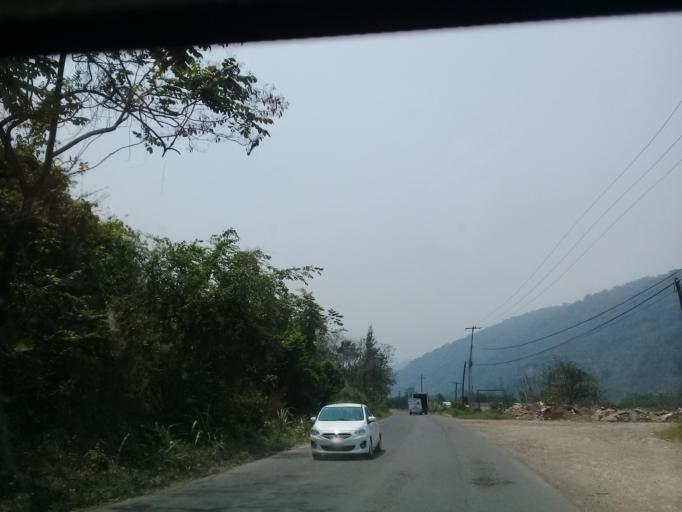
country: MX
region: Veracruz
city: Tezonapa
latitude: 18.6131
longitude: -96.6945
